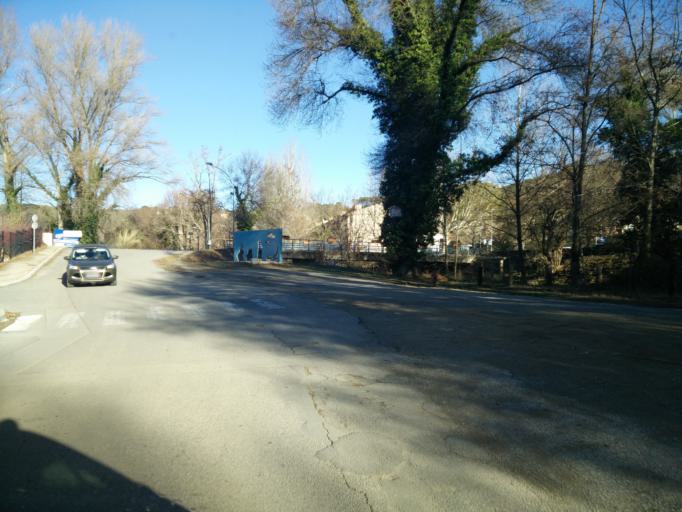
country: FR
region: Provence-Alpes-Cote d'Azur
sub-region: Departement du Var
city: Salernes
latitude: 43.5596
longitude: 6.2336
